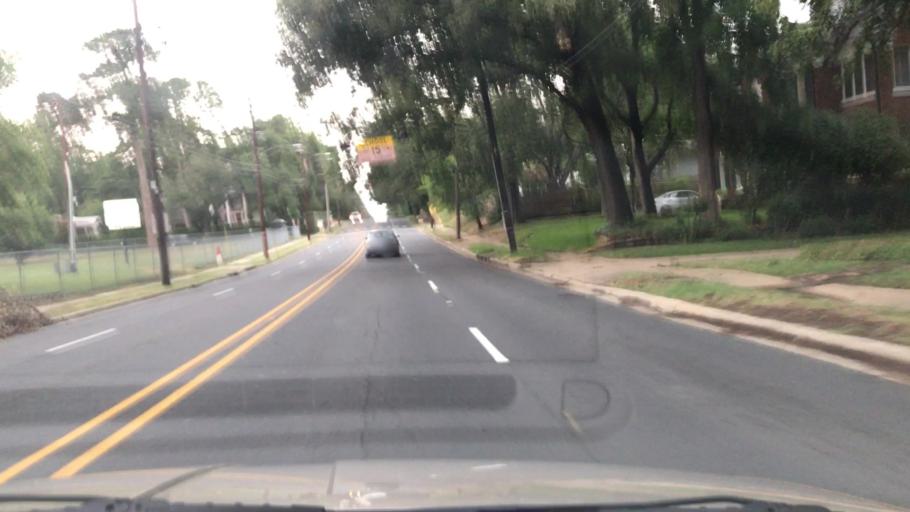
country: US
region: Louisiana
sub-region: Bossier Parish
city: Bossier City
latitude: 32.4596
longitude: -93.7460
